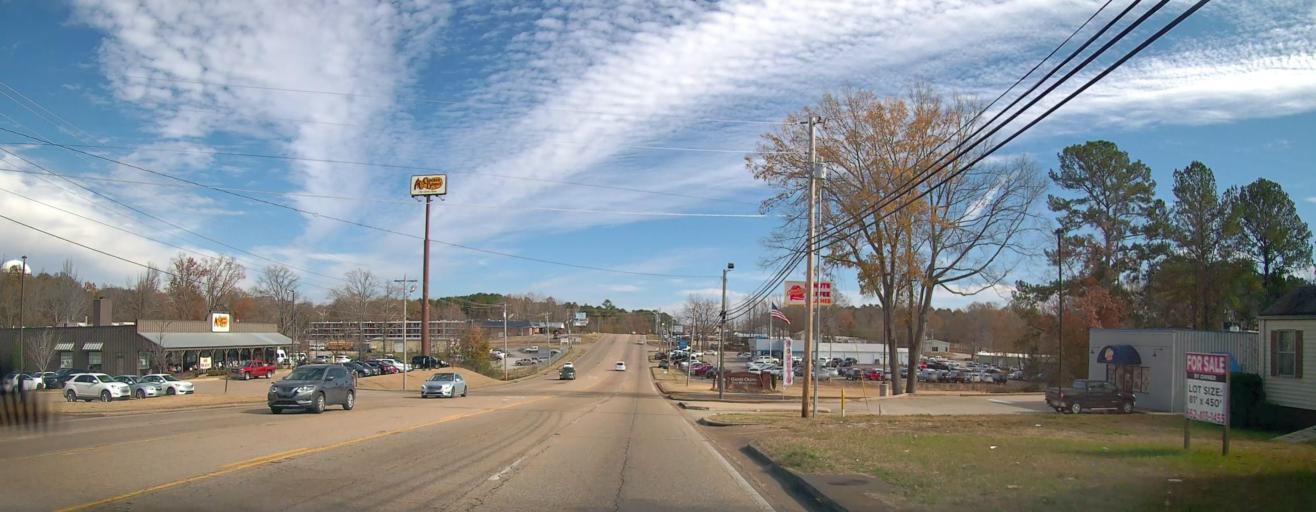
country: US
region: Mississippi
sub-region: Alcorn County
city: Corinth
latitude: 34.9307
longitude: -88.5442
